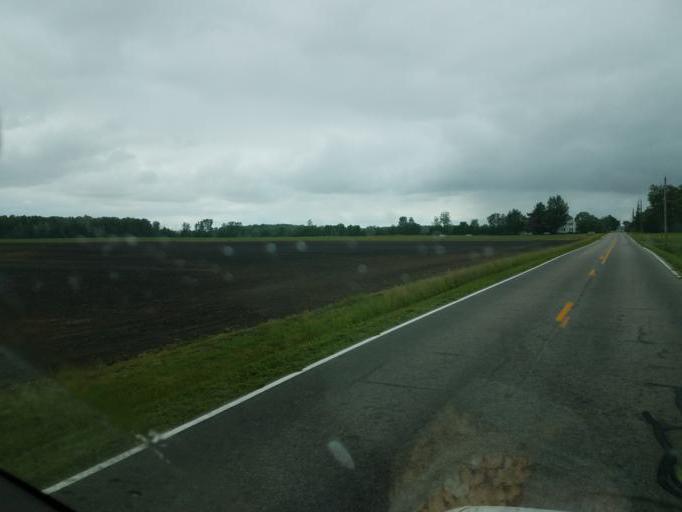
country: US
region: Ohio
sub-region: Marion County
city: Marion
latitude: 40.5642
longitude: -83.0273
